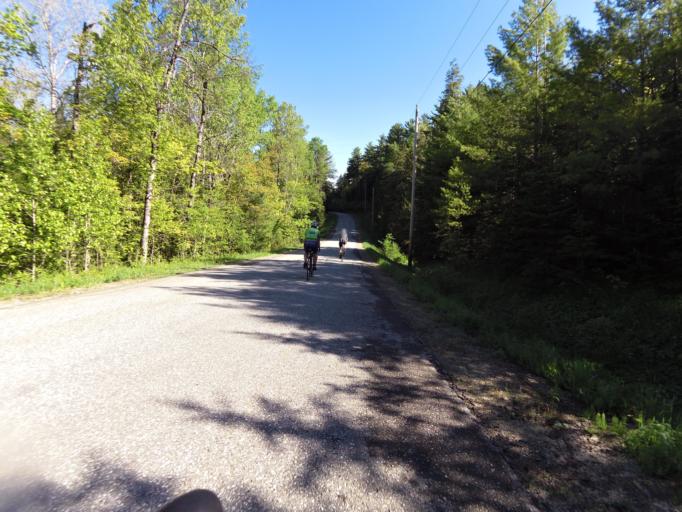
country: CA
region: Quebec
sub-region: Outaouais
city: Wakefield
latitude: 45.6145
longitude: -75.8812
